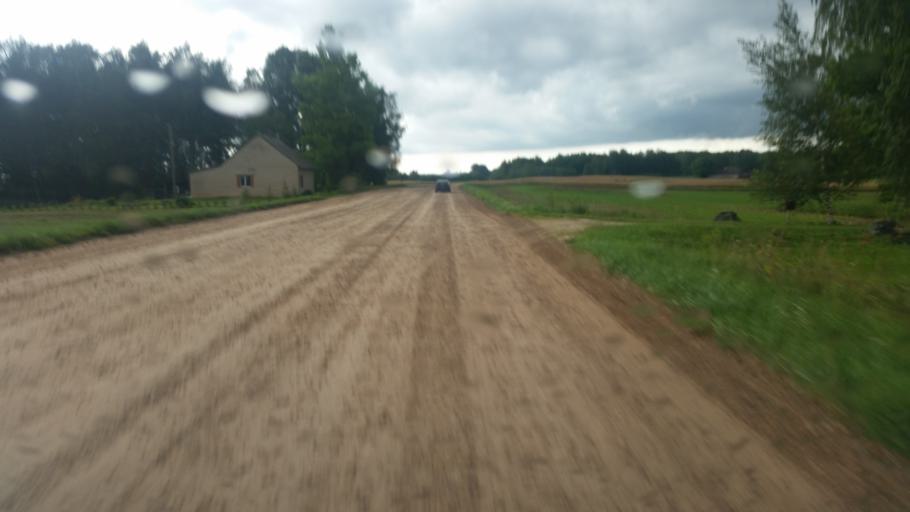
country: LV
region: Vecumnieki
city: Vecumnieki
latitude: 56.4261
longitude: 24.4842
